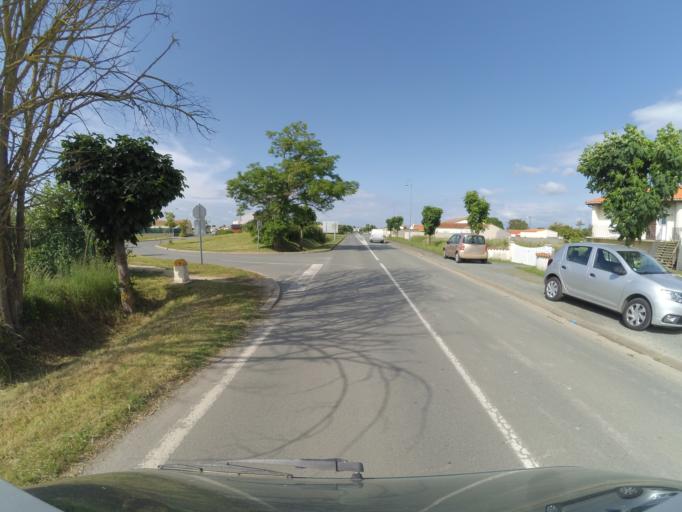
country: FR
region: Poitou-Charentes
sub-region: Departement de la Charente-Maritime
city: Saint-Xandre
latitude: 46.2360
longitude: -1.0721
